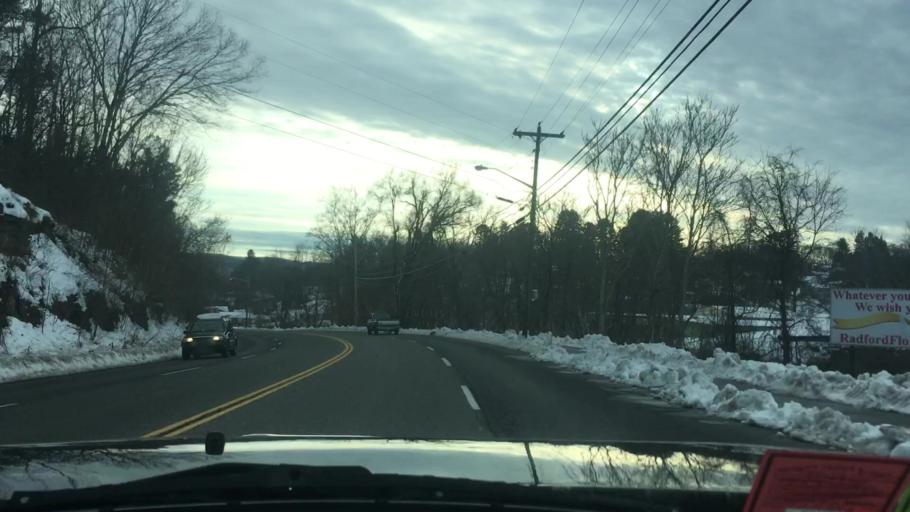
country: US
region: Virginia
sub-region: Pulaski County
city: Pulaski
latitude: 37.0616
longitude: -80.7716
